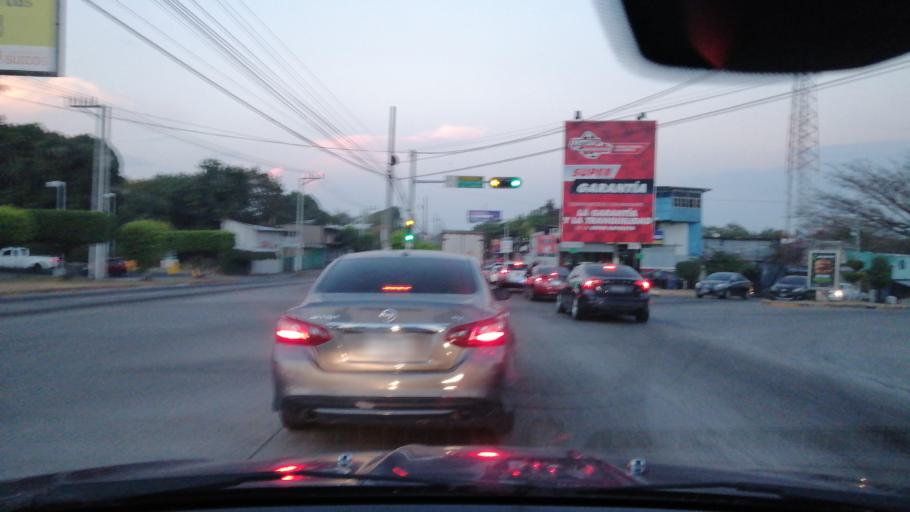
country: SV
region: San Salvador
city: Mejicanos
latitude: 13.7293
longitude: -89.2195
